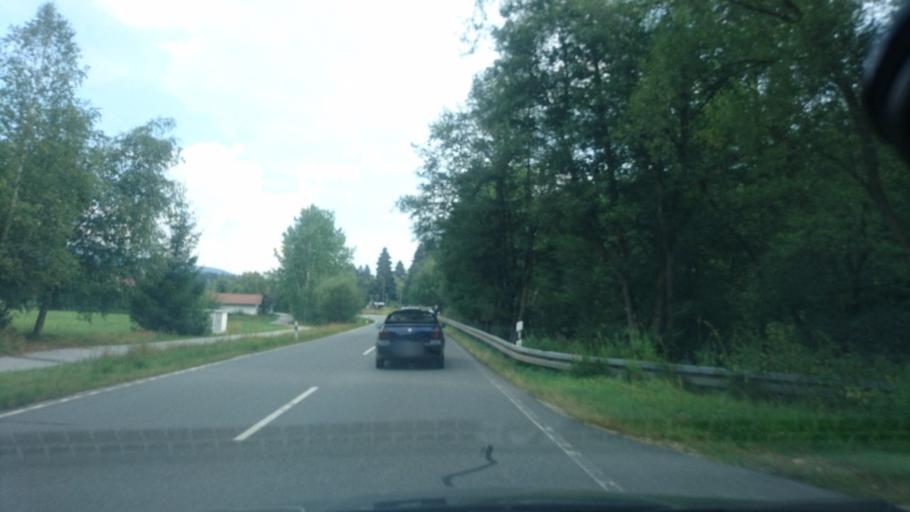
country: DE
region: Bavaria
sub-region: Lower Bavaria
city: Frauenau
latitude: 49.0083
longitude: 13.2755
